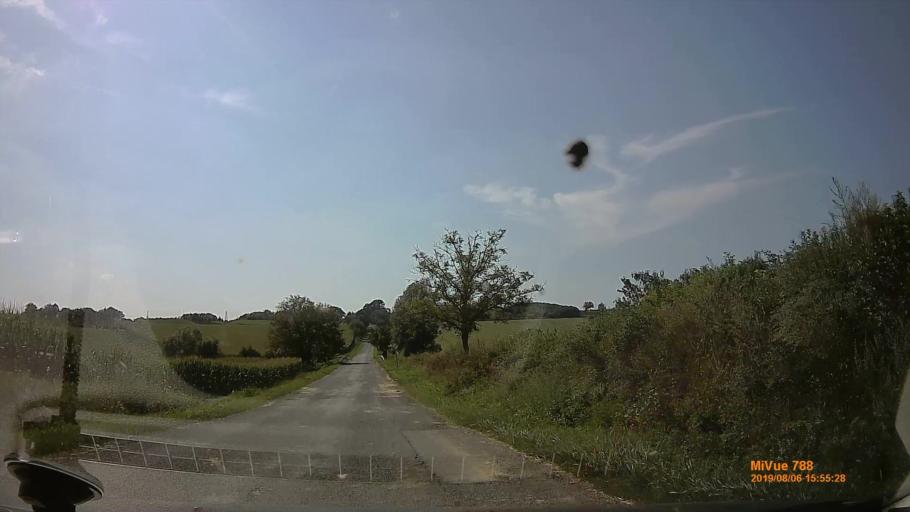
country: HU
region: Somogy
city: Csurgo
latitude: 46.2898
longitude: 17.0205
